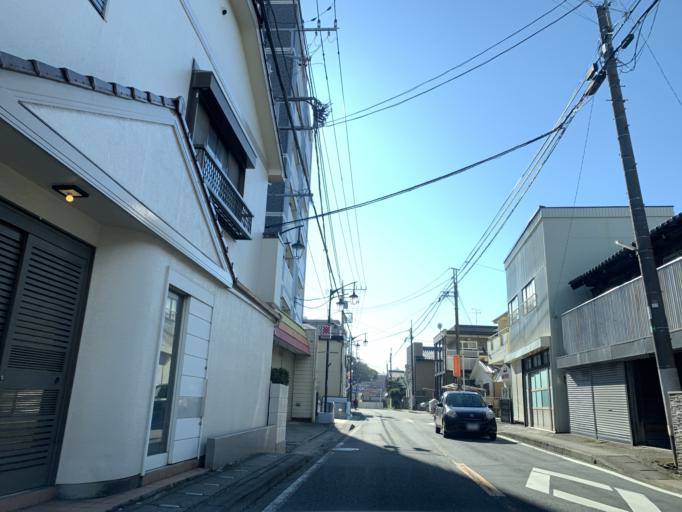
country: JP
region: Chiba
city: Matsudo
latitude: 35.7772
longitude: 139.8967
